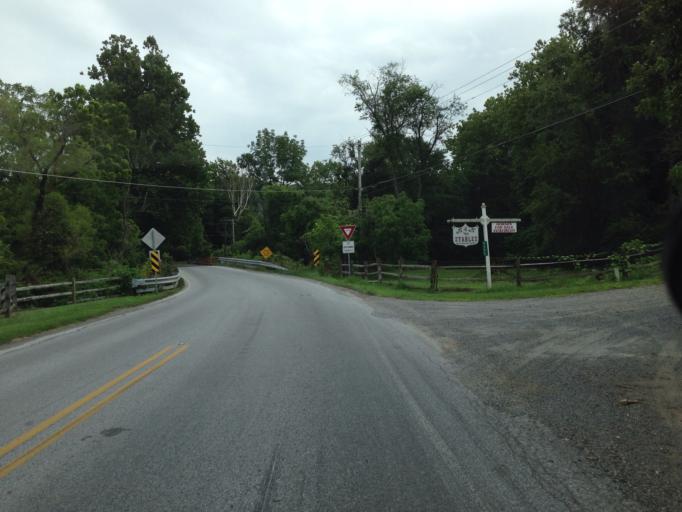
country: US
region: Pennsylvania
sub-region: Chester County
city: Oxford
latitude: 39.8601
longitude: -75.9797
